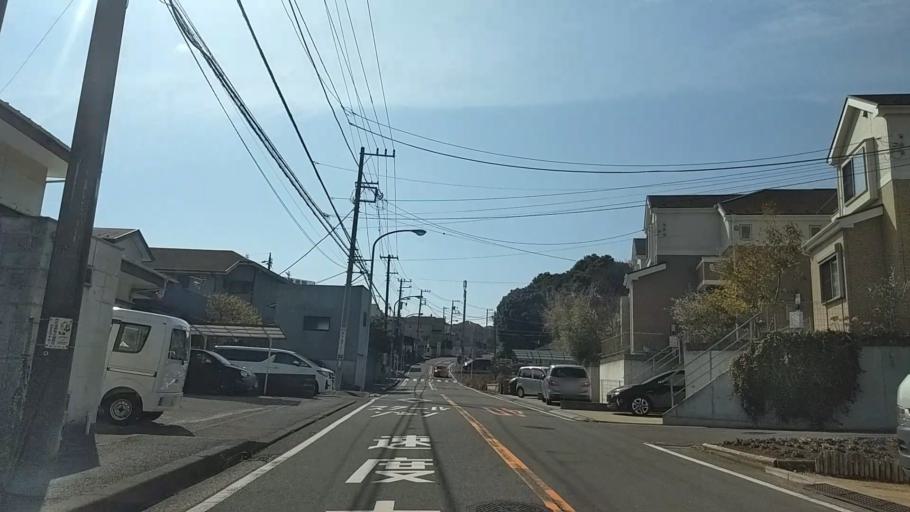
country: JP
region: Kanagawa
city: Kamakura
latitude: 35.3978
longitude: 139.5562
